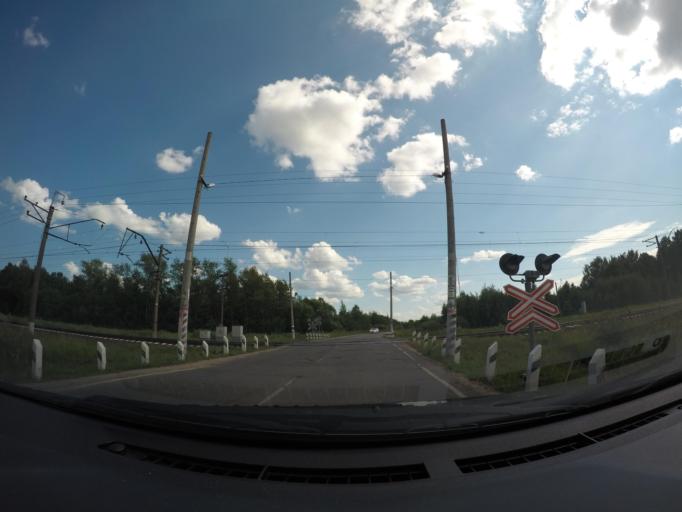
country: RU
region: Moskovskaya
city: Rechitsy
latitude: 55.6047
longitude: 38.5288
